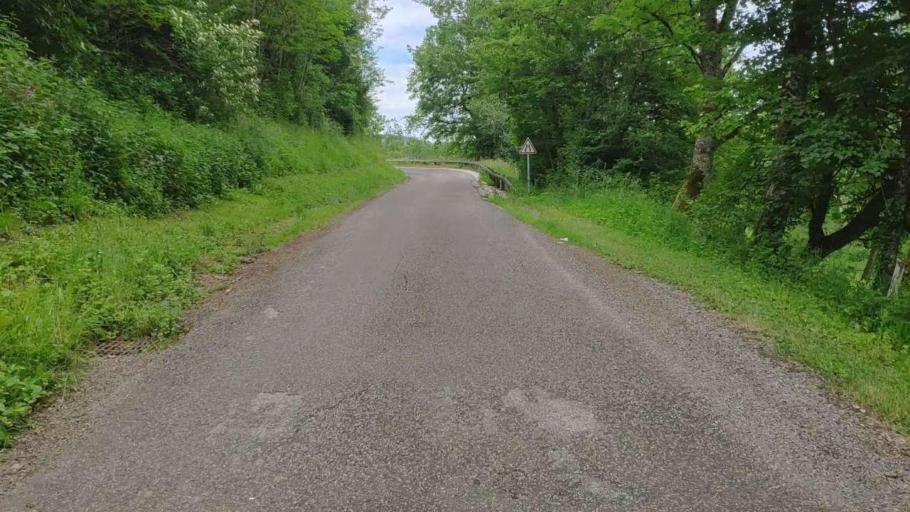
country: FR
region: Franche-Comte
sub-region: Departement du Jura
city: Perrigny
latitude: 46.7585
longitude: 5.5697
